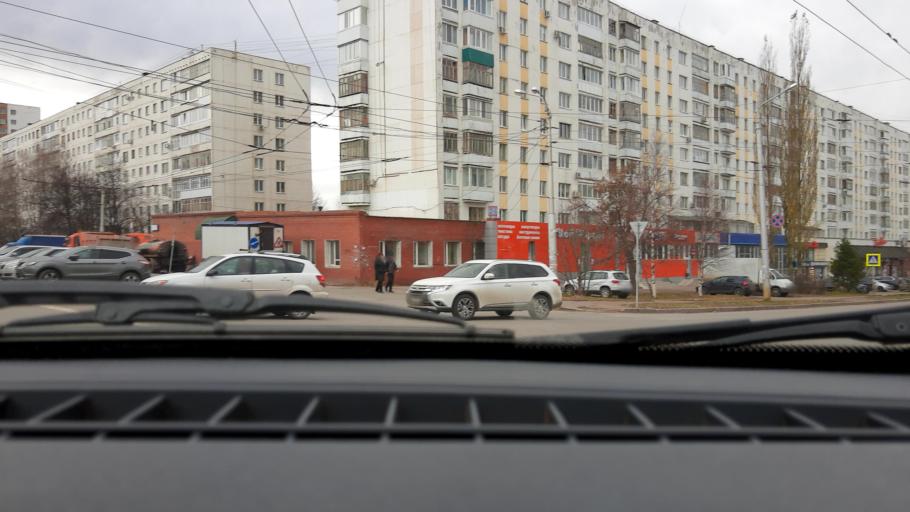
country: RU
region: Bashkortostan
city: Ufa
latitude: 54.7402
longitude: 56.0280
